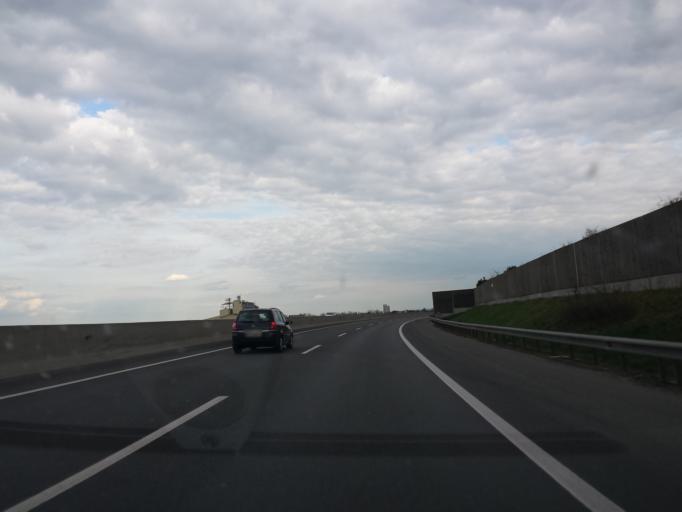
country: AT
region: Lower Austria
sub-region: Politischer Bezirk Tulln
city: Grafenworth
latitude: 48.4117
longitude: 15.7833
